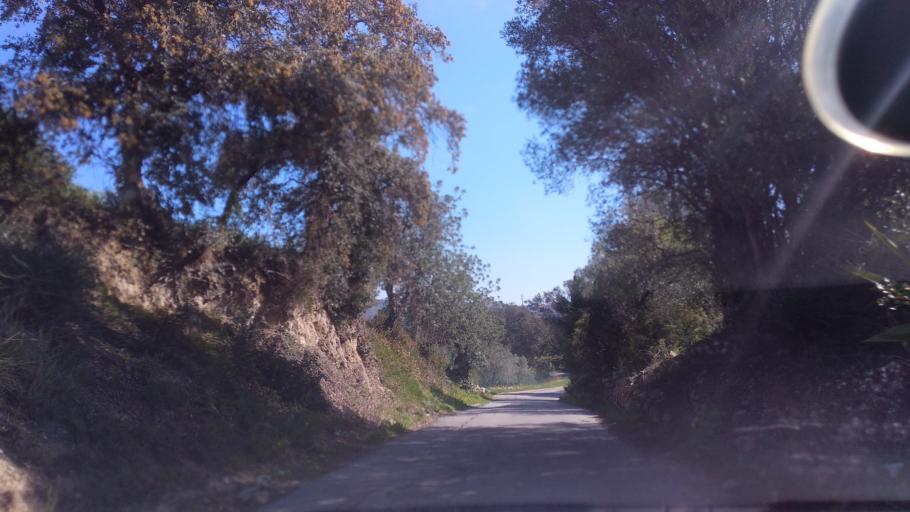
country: PT
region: Faro
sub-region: Faro
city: Santa Barbara de Nexe
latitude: 37.1117
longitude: -7.9242
